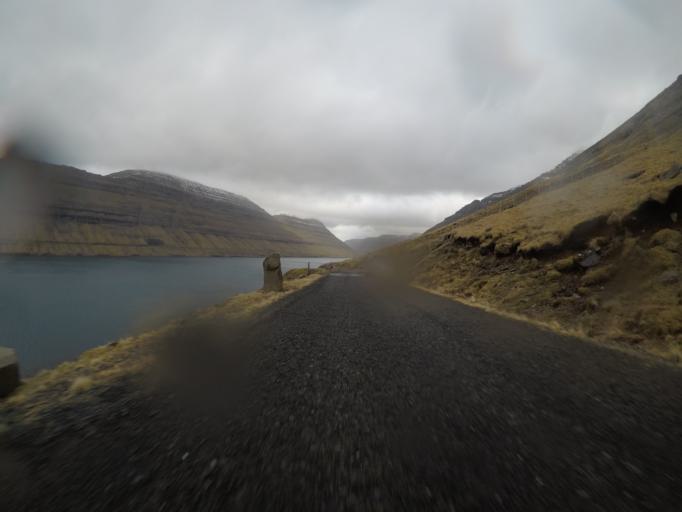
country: FO
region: Nordoyar
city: Klaksvik
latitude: 62.3263
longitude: -6.5660
